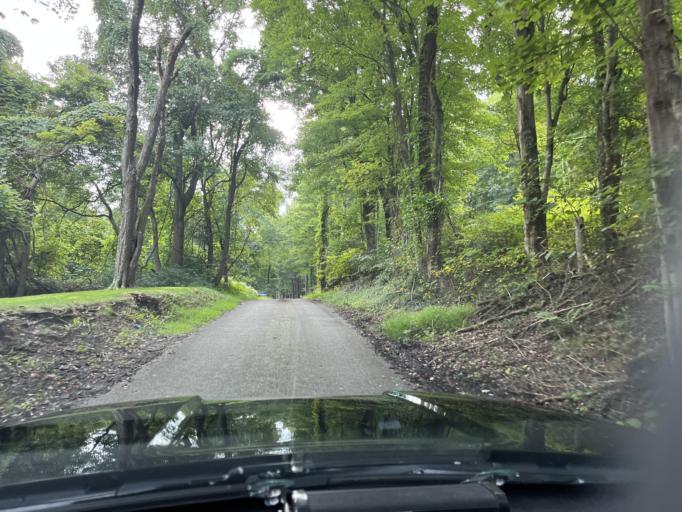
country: US
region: Pennsylvania
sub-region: Fayette County
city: Hopwood
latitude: 39.8634
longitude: -79.6931
